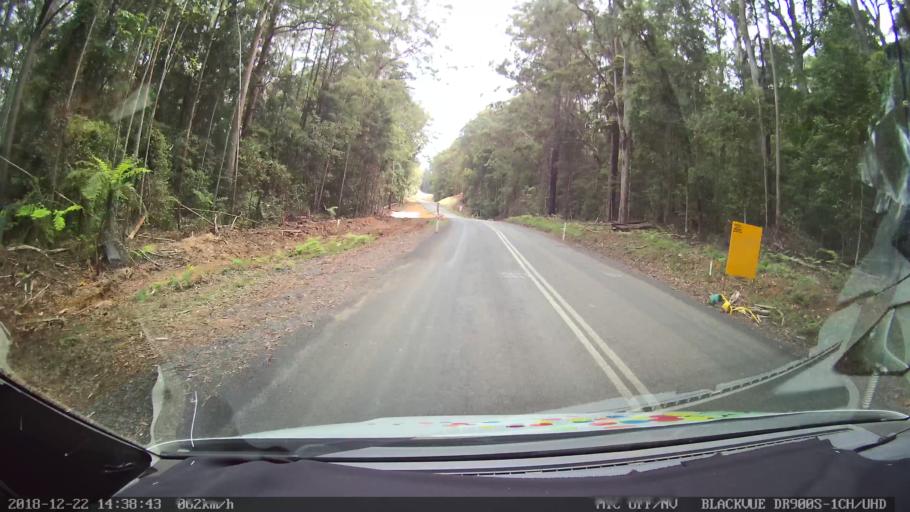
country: AU
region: New South Wales
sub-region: Bellingen
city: Dorrigo
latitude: -30.1404
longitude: 152.5957
